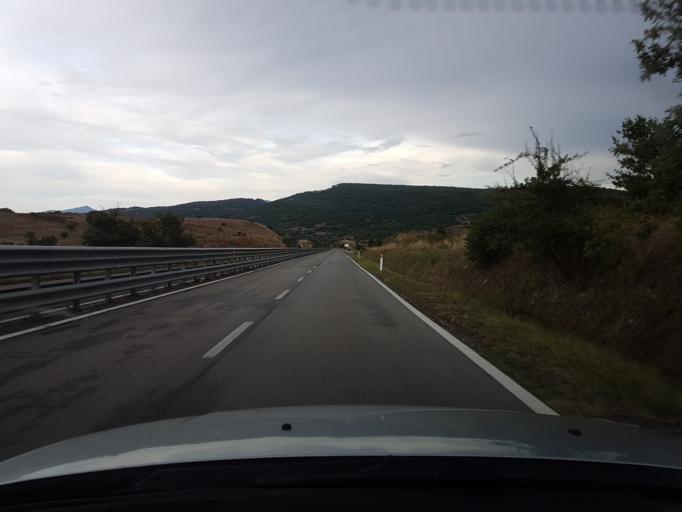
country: IT
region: Sardinia
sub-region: Provincia di Oristano
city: Sedilo
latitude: 40.1801
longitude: 8.9489
